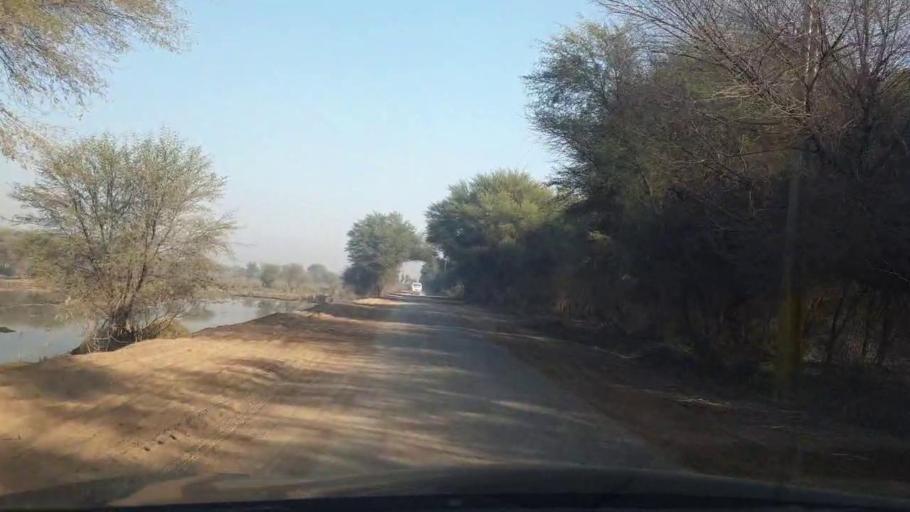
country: PK
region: Sindh
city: Mirpur Mathelo
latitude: 28.0626
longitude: 69.4644
